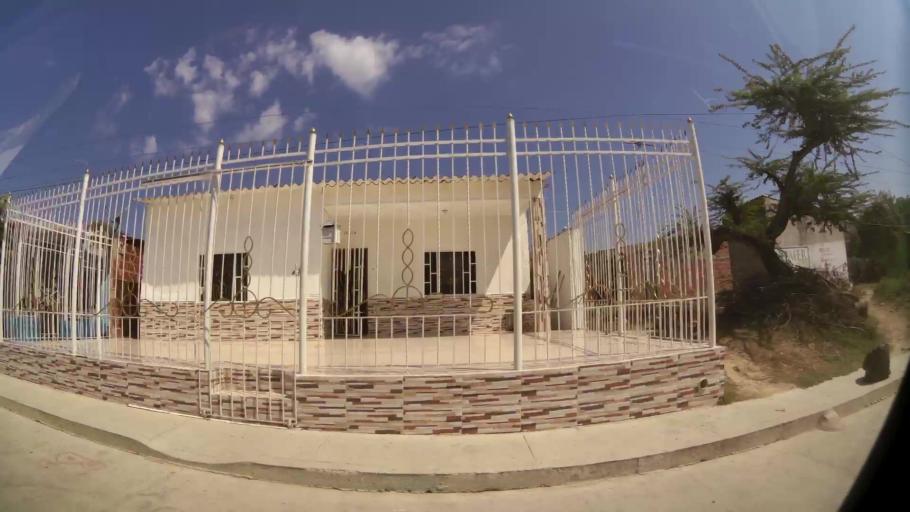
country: CO
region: Atlantico
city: Barranquilla
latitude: 10.9667
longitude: -74.8206
